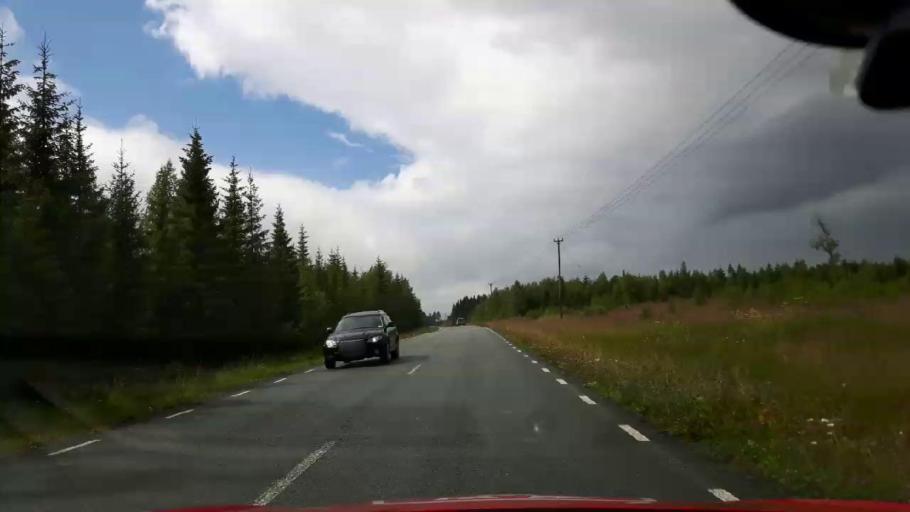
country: SE
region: Jaemtland
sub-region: Krokoms Kommun
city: Krokom
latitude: 63.3507
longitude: 14.2188
